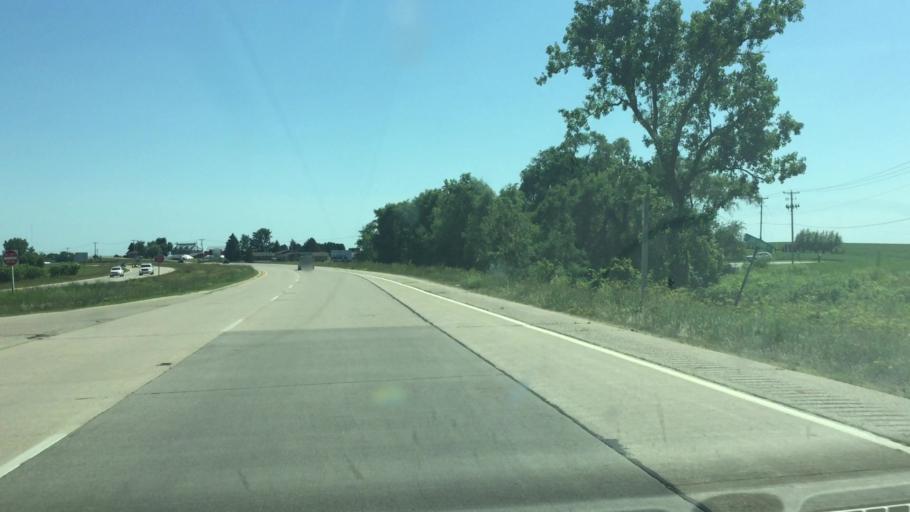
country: US
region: Wisconsin
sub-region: Grant County
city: Dickeyville
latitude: 42.5742
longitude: -90.6111
